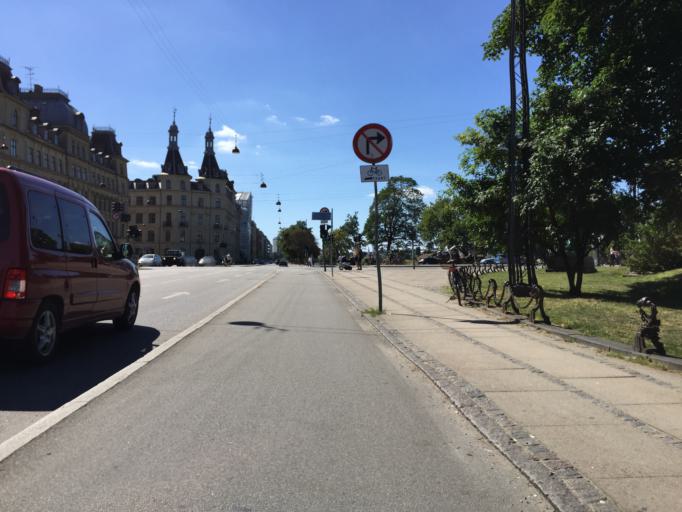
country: DK
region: Capital Region
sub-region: Kobenhavn
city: Copenhagen
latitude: 55.6866
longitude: 12.5656
